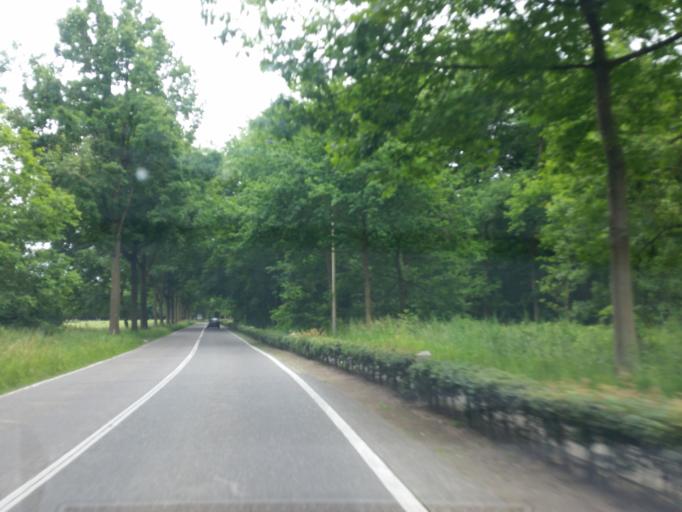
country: BE
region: Flanders
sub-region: Provincie Antwerpen
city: Schilde
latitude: 51.2222
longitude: 4.5992
